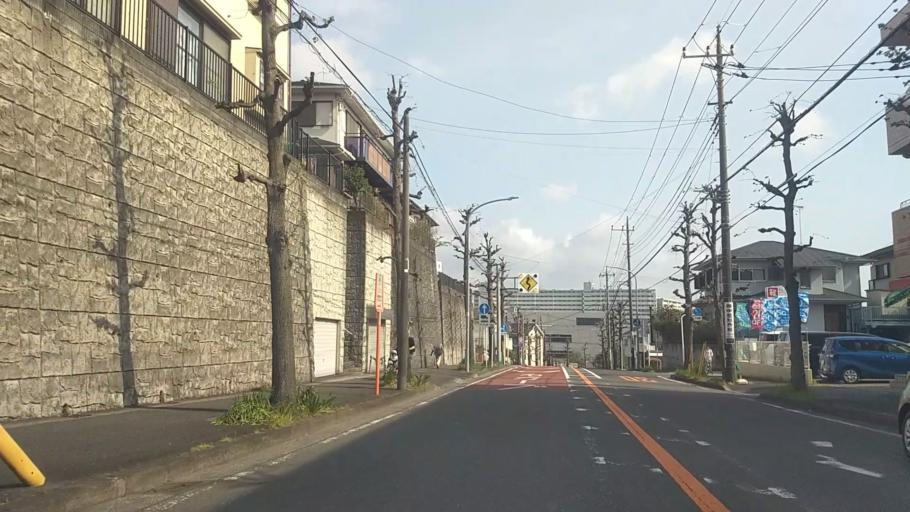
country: JP
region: Kanagawa
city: Kamakura
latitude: 35.3708
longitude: 139.5469
